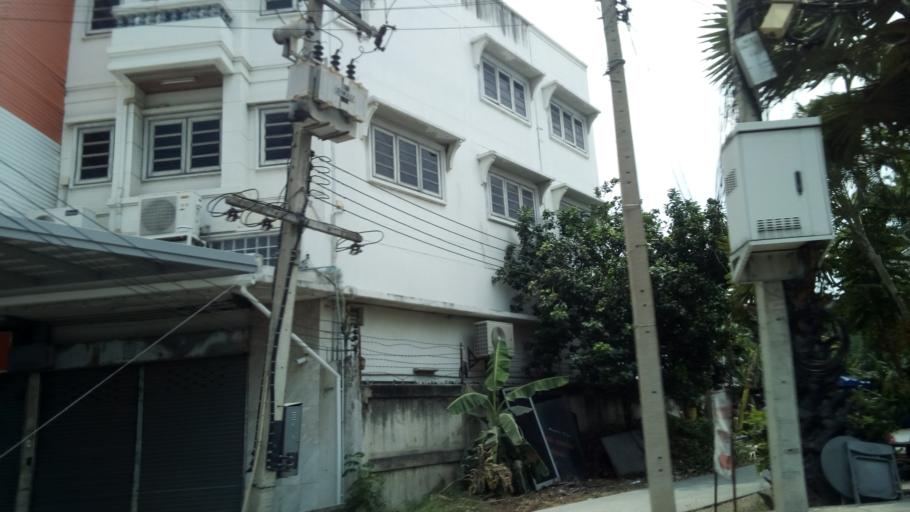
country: TH
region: Phra Nakhon Si Ayutthaya
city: Phra Nakhon Si Ayutthaya
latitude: 14.3523
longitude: 100.6006
